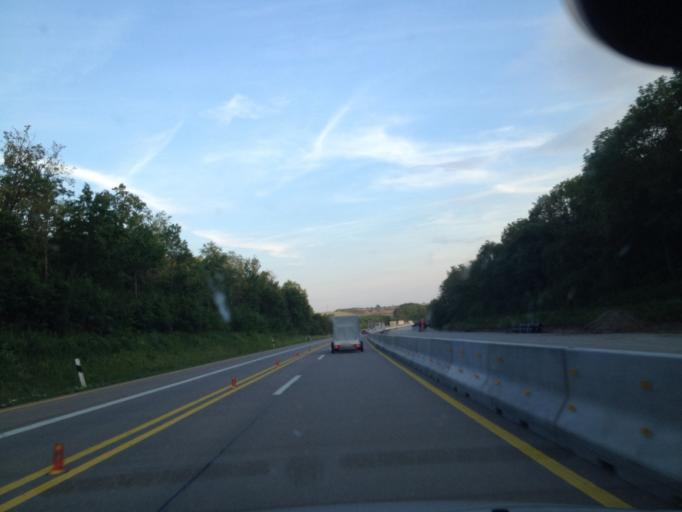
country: DE
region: Bavaria
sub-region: Regierungsbezirk Mittelfranken
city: Gollhofen
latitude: 49.5750
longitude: 10.1725
